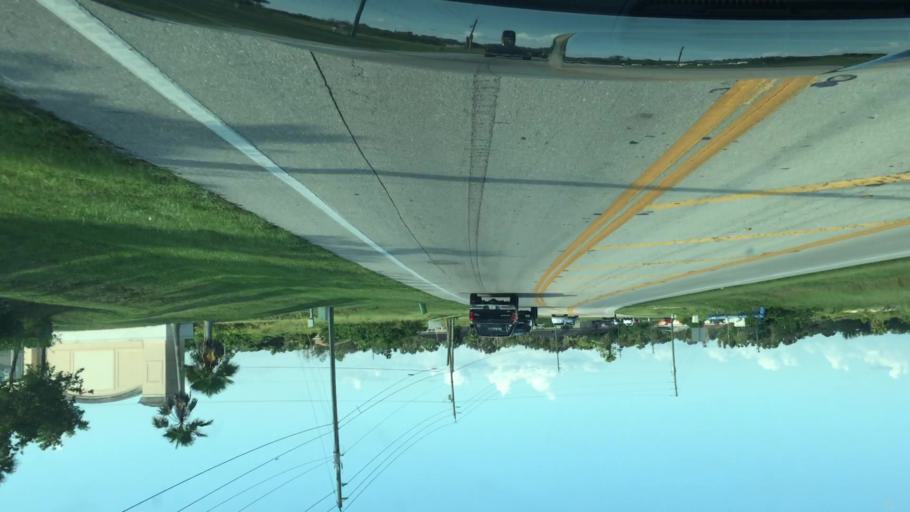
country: US
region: Florida
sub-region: Lee County
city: Gateway
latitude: 26.6140
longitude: -81.7487
